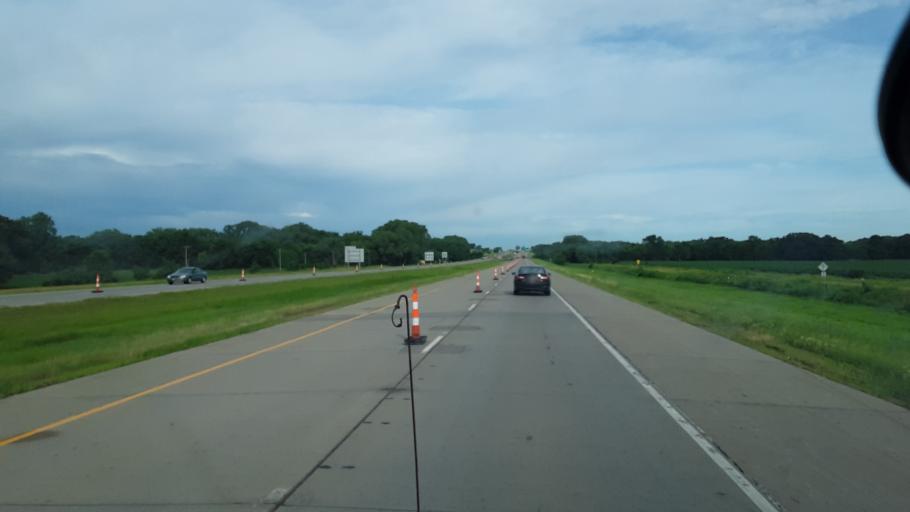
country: US
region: South Dakota
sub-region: Minnehaha County
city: Sioux Falls
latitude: 43.6088
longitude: -96.7362
